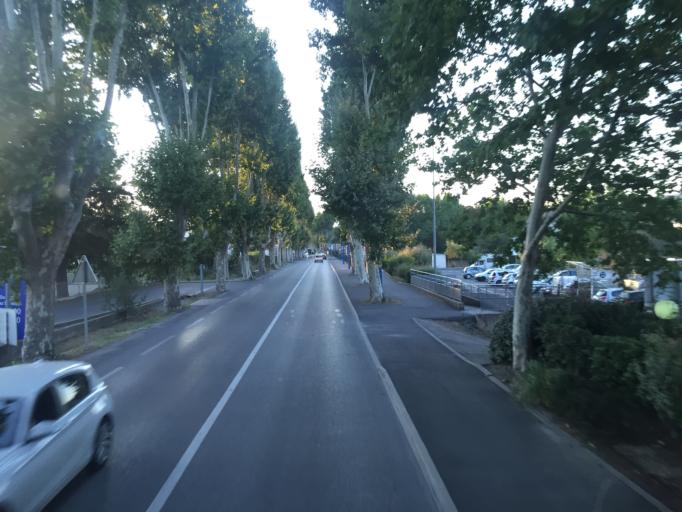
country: FR
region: Provence-Alpes-Cote d'Azur
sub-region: Departement des Alpes-de-Haute-Provence
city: Manosque
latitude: 43.8181
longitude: 5.7977
